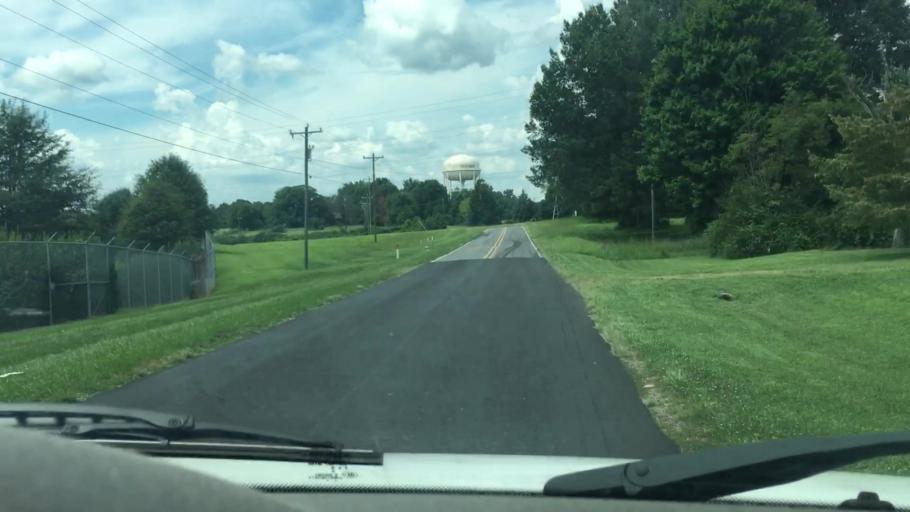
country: US
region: North Carolina
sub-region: Iredell County
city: Troutman
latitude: 35.6777
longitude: -80.8475
